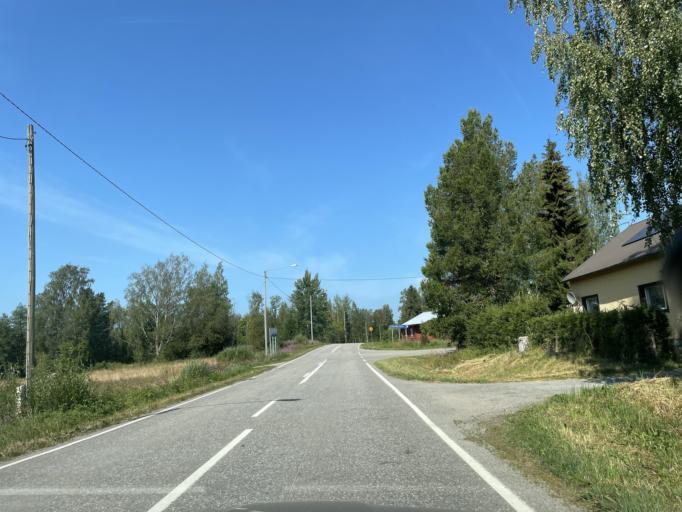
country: FI
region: Central Finland
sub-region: Saarijaervi-Viitasaari
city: Pihtipudas
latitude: 63.3580
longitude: 25.7523
